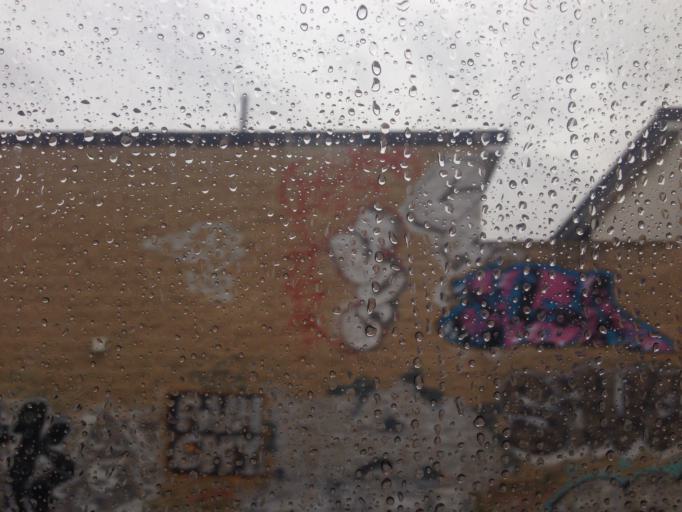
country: GB
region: England
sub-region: Greater London
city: Battersea
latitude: 51.4704
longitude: -0.1667
